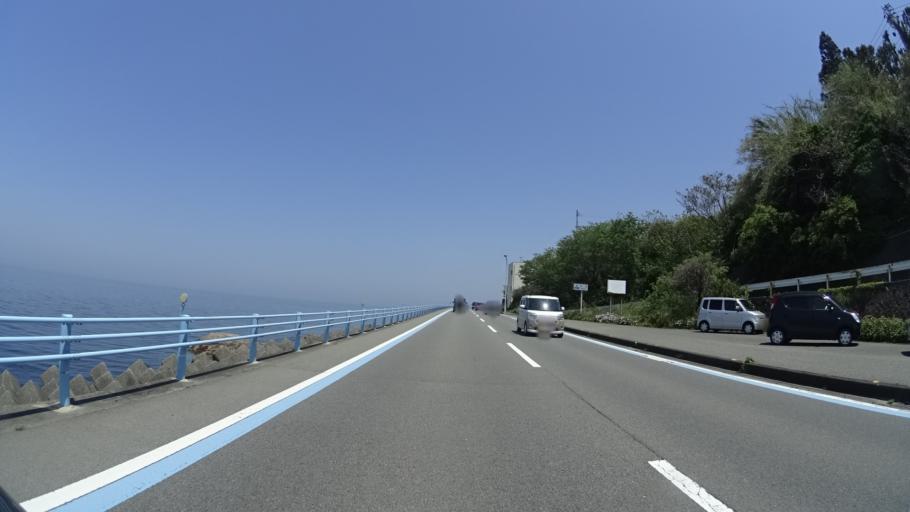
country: JP
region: Ehime
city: Iyo
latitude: 33.6713
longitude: 132.6107
